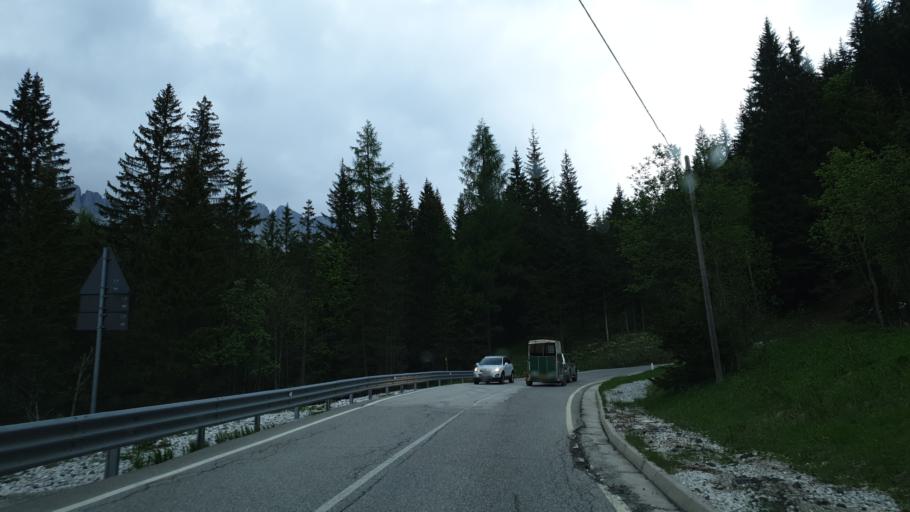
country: IT
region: Veneto
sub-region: Provincia di Belluno
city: San Vito
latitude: 46.5553
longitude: 12.2454
